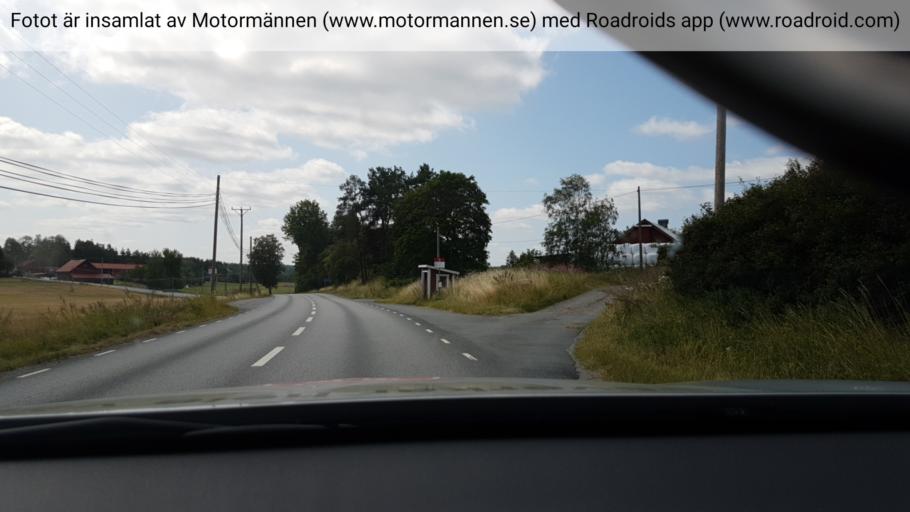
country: SE
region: Stockholm
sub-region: Vallentuna Kommun
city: Vallentuna
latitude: 59.5424
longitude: 18.1720
